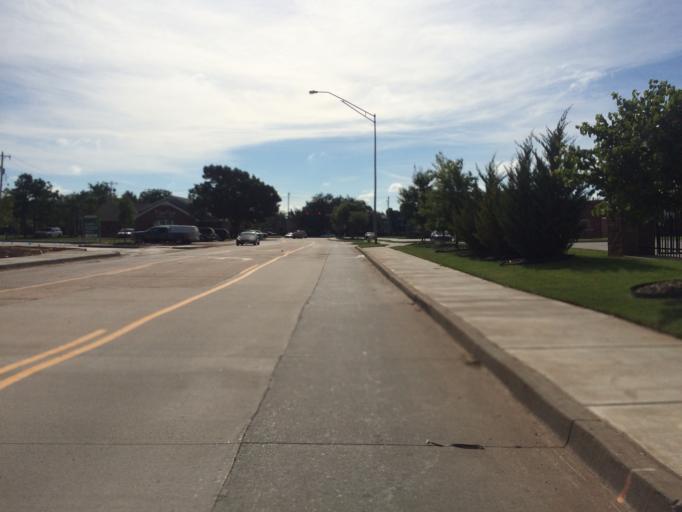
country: US
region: Oklahoma
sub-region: Cleveland County
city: Norman
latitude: 35.2231
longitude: -97.4785
